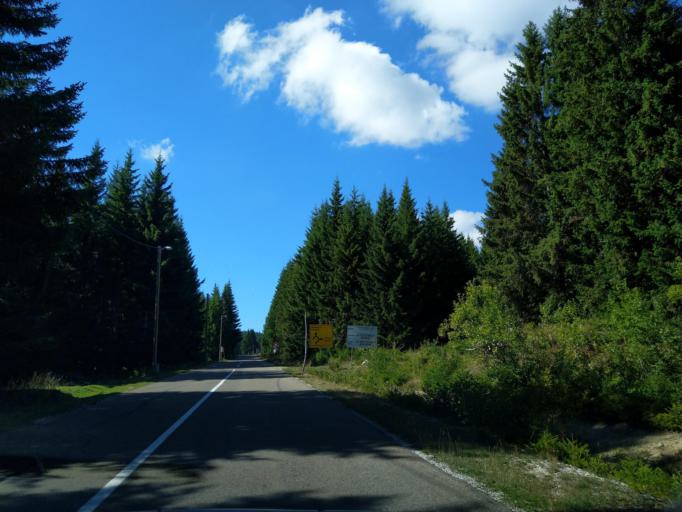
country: RS
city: Sokolovica
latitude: 43.2756
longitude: 20.3476
